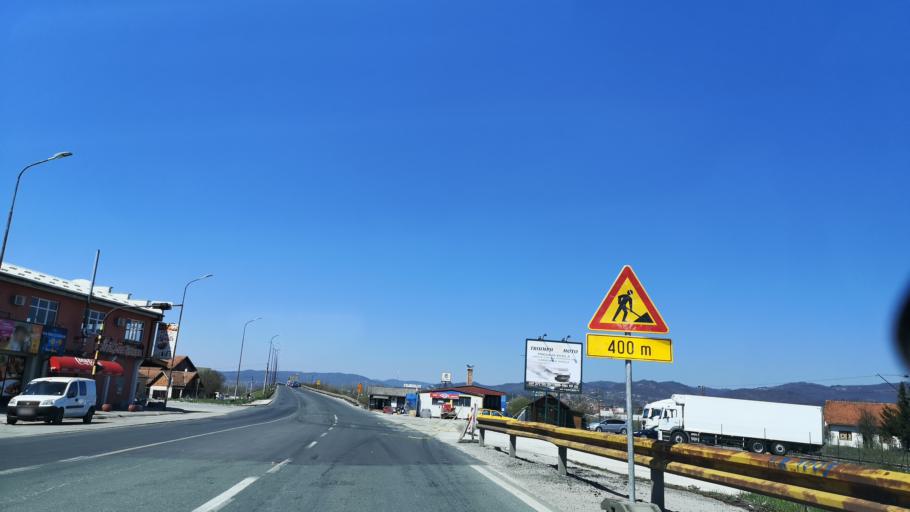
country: RS
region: Central Serbia
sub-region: Zlatiborski Okrug
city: Pozega
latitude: 43.8316
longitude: 20.0417
